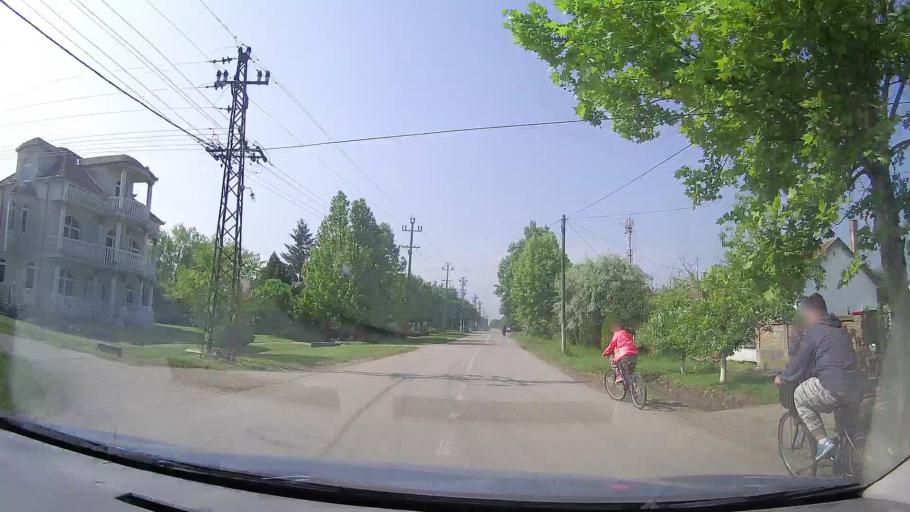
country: RS
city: Jasa Tomic
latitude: 45.4478
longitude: 20.8550
